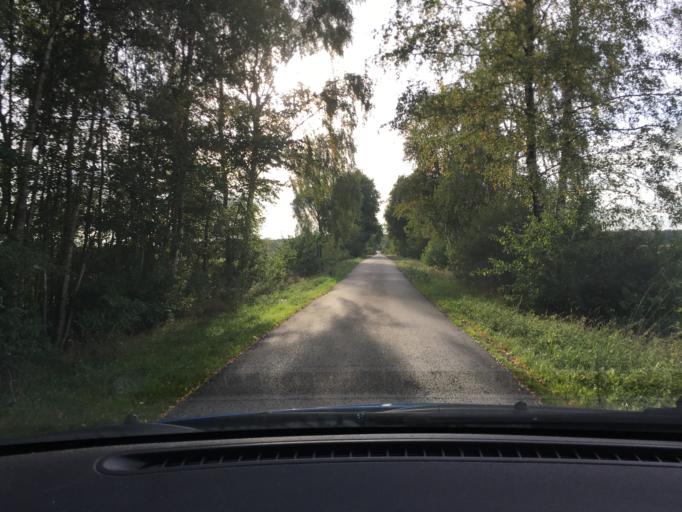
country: DE
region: Lower Saxony
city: Wietzendorf
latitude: 52.8899
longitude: 9.9308
